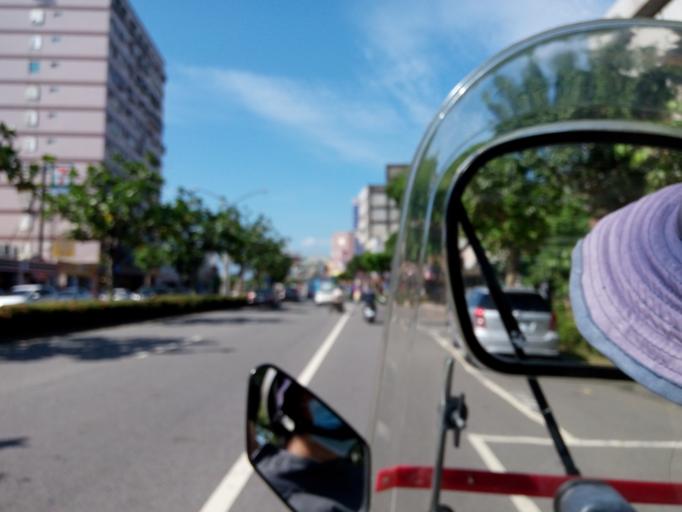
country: TW
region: Taiwan
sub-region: Yilan
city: Yilan
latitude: 24.6807
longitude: 121.7617
